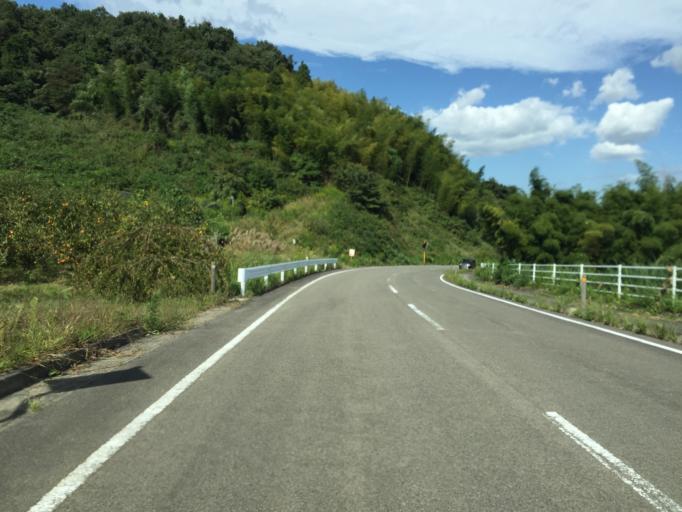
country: JP
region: Fukushima
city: Hobaramachi
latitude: 37.7772
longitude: 140.5377
